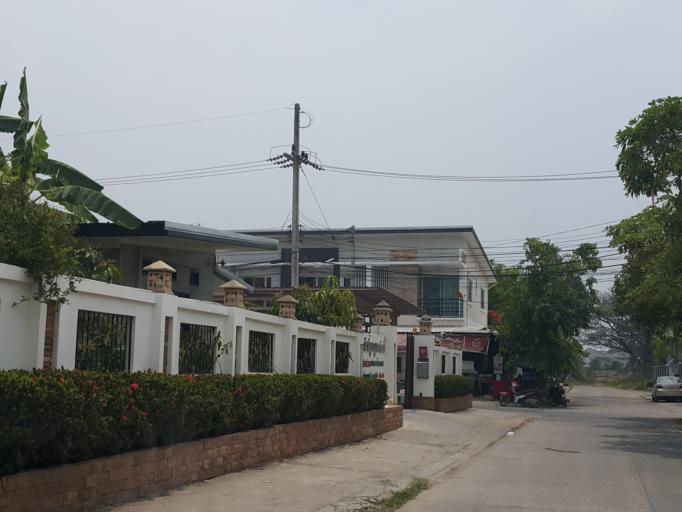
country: TH
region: Chiang Mai
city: Saraphi
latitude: 18.7509
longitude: 99.0367
